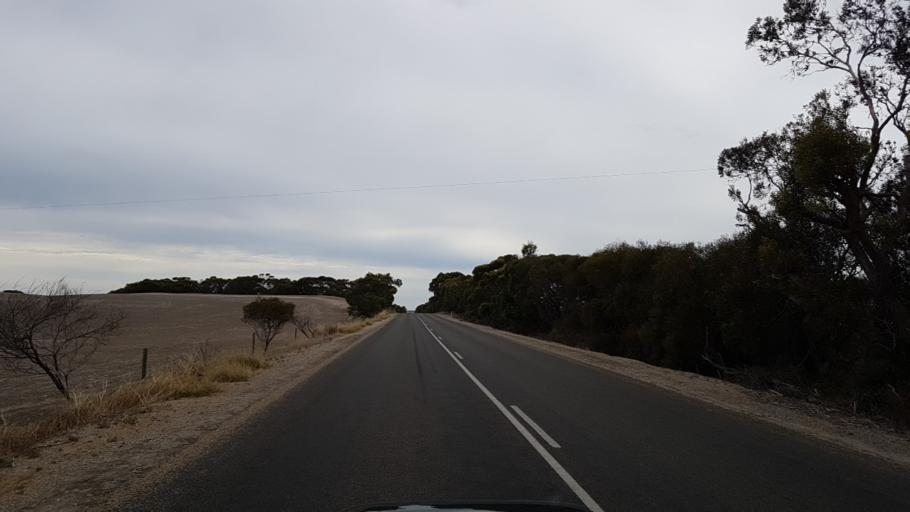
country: AU
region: South Australia
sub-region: Yorke Peninsula
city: Honiton
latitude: -34.9870
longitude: 137.1473
